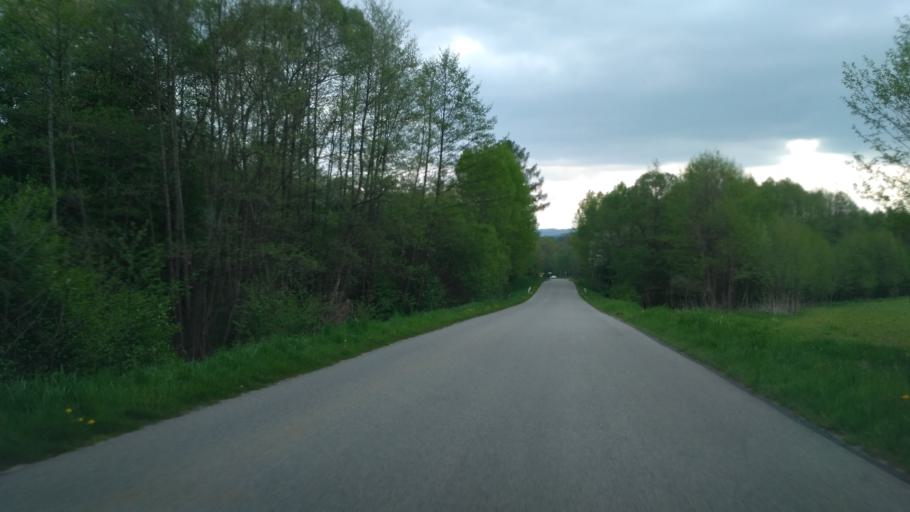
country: PL
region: Subcarpathian Voivodeship
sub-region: Powiat debicki
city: Leki Gorne
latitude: 49.9810
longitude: 21.1565
